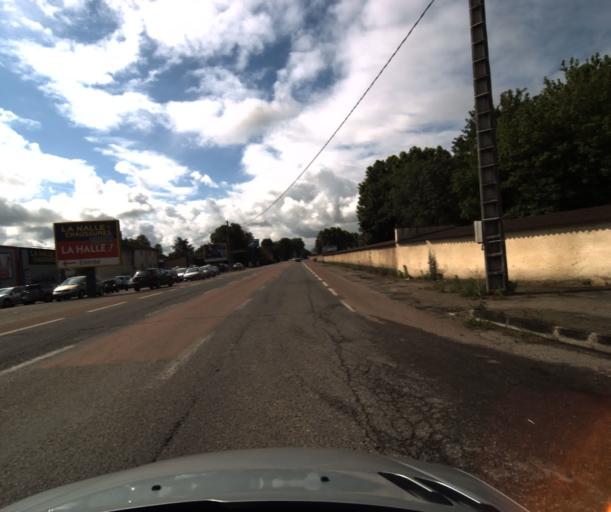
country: FR
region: Midi-Pyrenees
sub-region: Departement du Tarn-et-Garonne
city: Castelsarrasin
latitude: 44.0613
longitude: 1.0979
